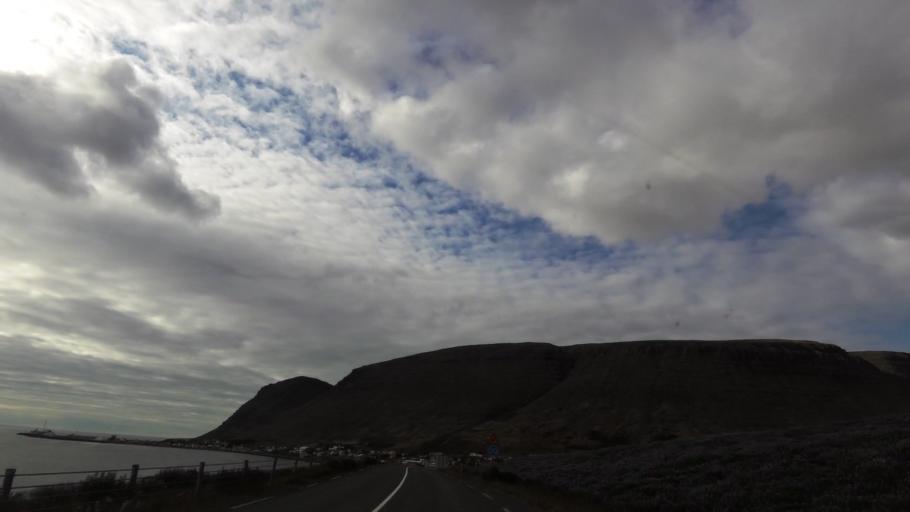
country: IS
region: West
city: Olafsvik
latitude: 65.5863
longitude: -23.9691
